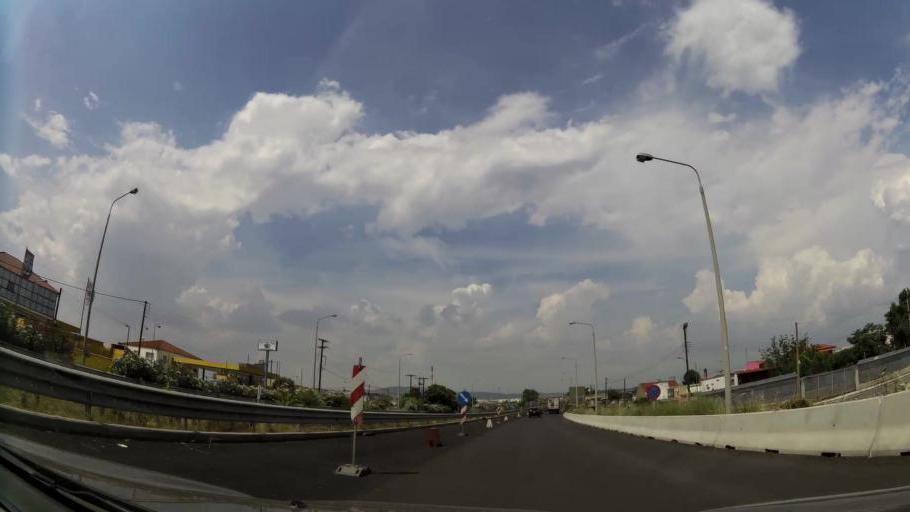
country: GR
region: Central Macedonia
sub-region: Nomos Thessalonikis
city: Menemeni
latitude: 40.6669
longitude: 22.8827
